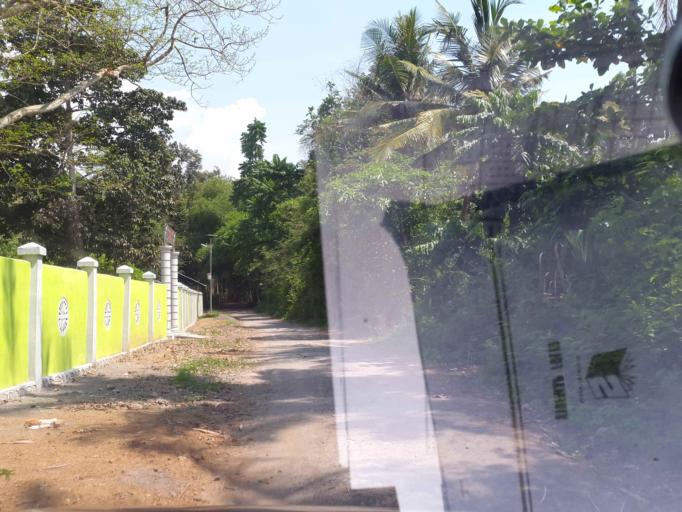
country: ID
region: West Nusa Tenggara
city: Karangkebon Timur
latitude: -8.6774
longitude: 116.0894
